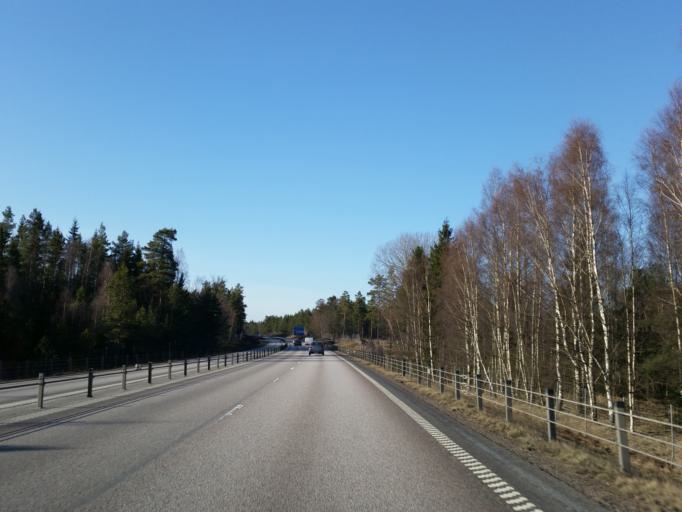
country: SE
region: Kalmar
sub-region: Oskarshamns Kommun
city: Oskarshamn
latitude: 57.2355
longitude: 16.4360
